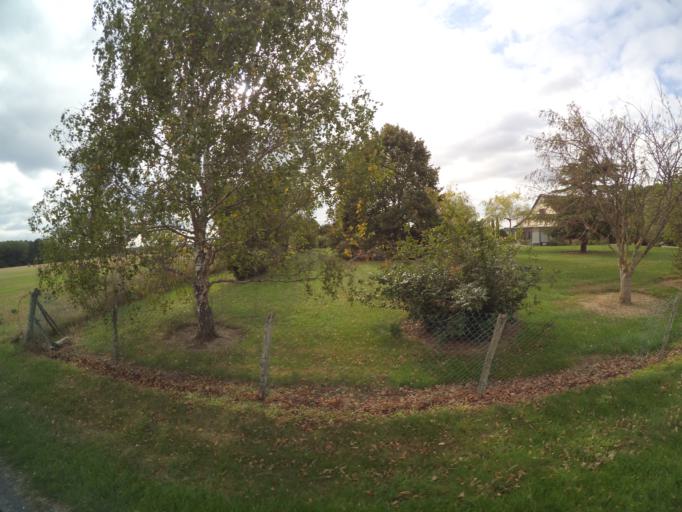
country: FR
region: Centre
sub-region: Departement d'Indre-et-Loire
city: Nazelles-Negron
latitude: 47.4819
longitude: 0.9398
